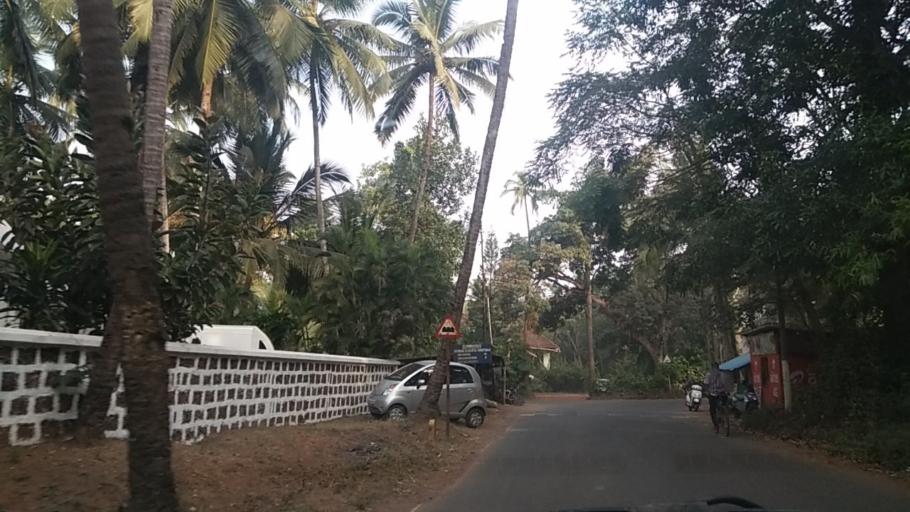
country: IN
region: Goa
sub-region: South Goa
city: Benaulim
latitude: 15.2654
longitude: 73.9445
